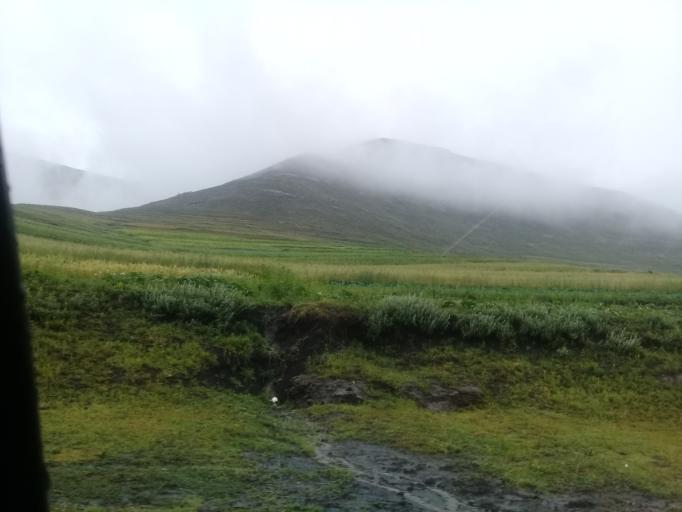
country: LS
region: Mokhotlong
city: Mokhotlong
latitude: -29.3873
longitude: 28.9512
